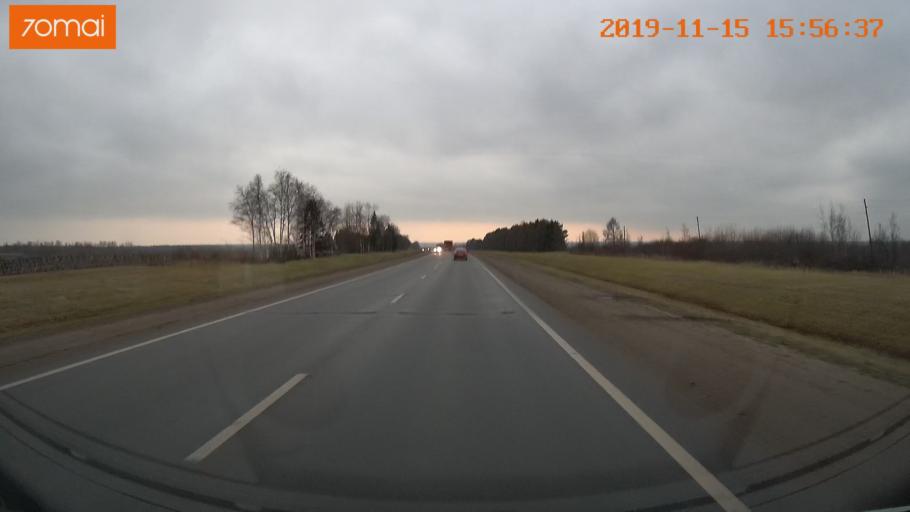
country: RU
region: Jaroslavl
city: Yaroslavl
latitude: 57.8401
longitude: 39.9716
